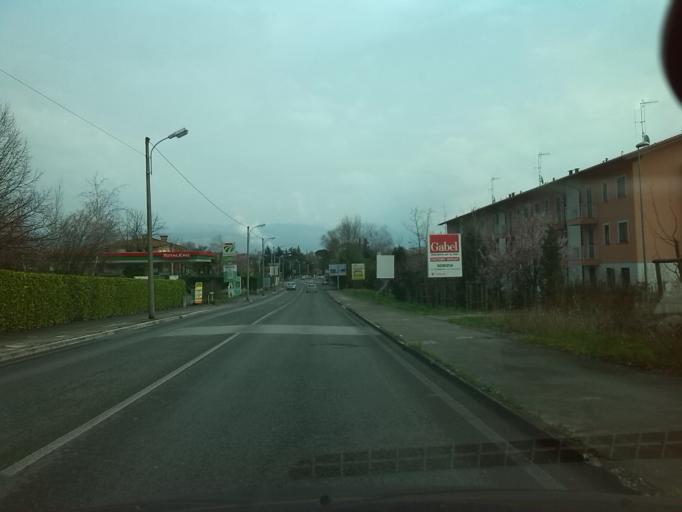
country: IT
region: Friuli Venezia Giulia
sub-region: Provincia di Gorizia
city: Savogna d'Isonzo
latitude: 45.9364
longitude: 13.5836
